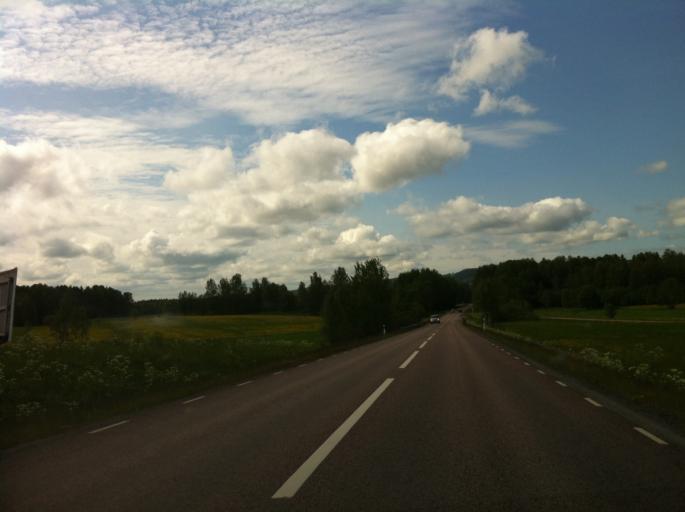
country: SE
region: Vaermland
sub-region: Sunne Kommun
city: Sunne
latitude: 59.6981
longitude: 13.1463
